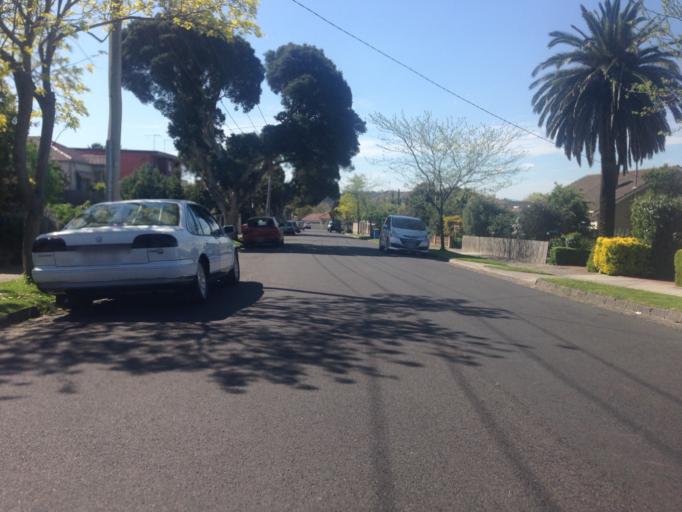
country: AU
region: Victoria
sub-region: Boroondara
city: Kew East
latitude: -37.7937
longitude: 145.0531
